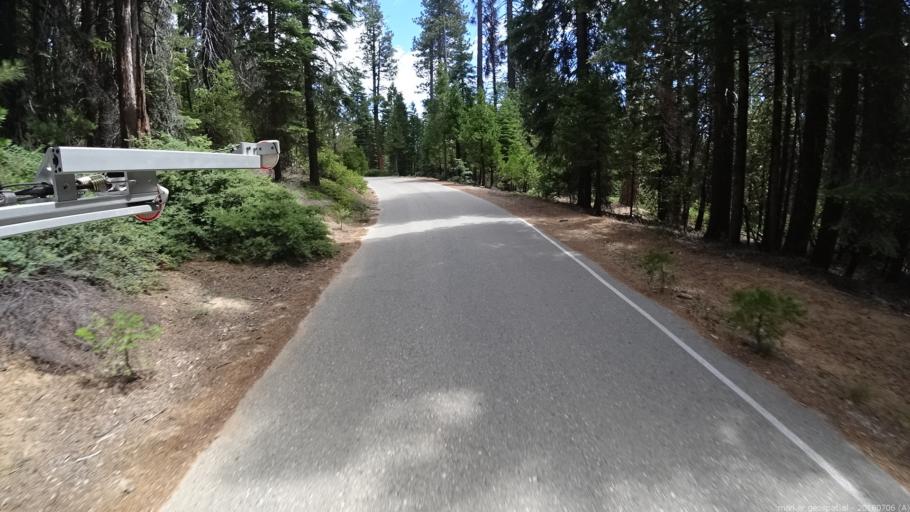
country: US
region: California
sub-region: Madera County
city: Oakhurst
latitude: 37.4201
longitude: -119.4138
